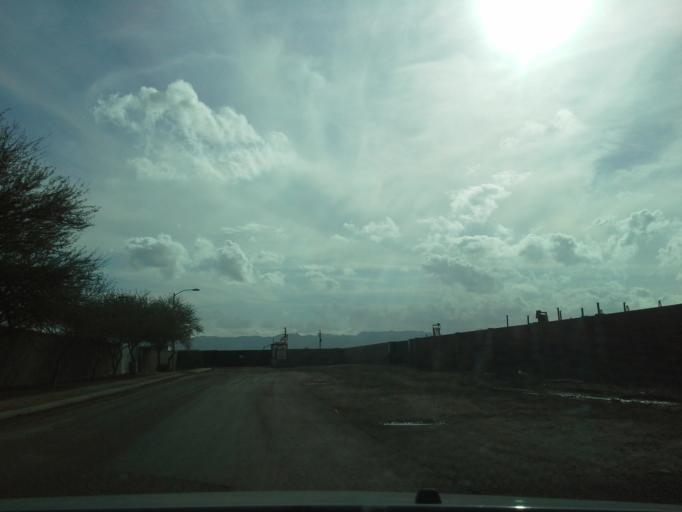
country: US
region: Arizona
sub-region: Maricopa County
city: Phoenix
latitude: 33.4237
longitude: -112.0868
